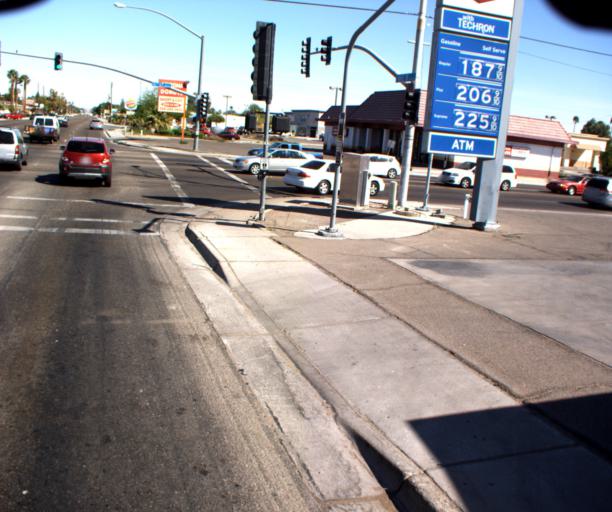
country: US
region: Arizona
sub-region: Yuma County
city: Yuma
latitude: 32.6982
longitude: -114.6503
